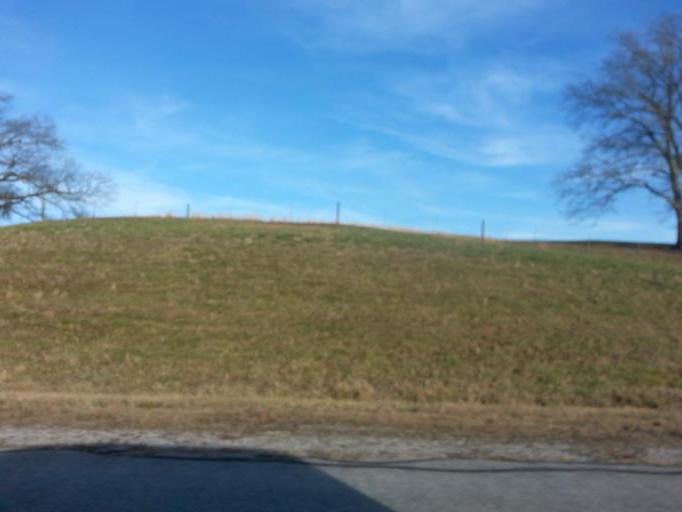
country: US
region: Tennessee
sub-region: White County
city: Sparta
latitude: 35.9009
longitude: -85.4728
